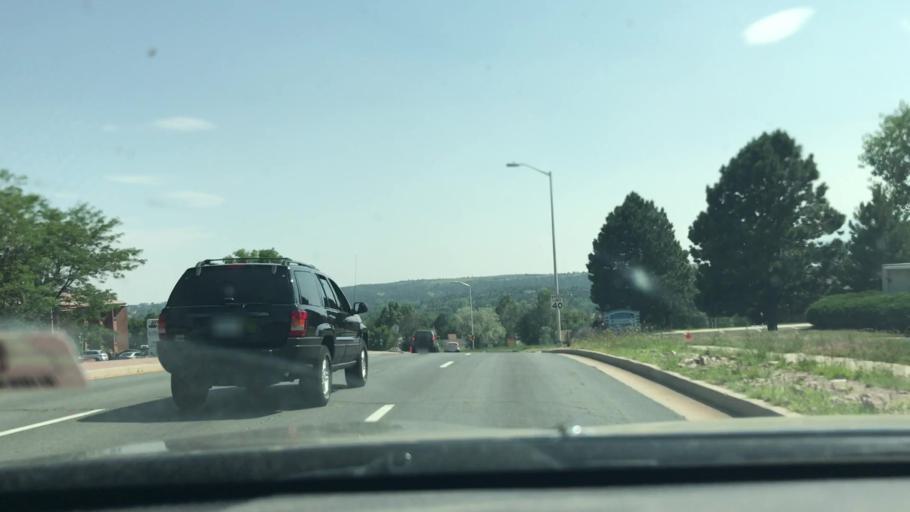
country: US
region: Colorado
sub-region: El Paso County
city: Colorado Springs
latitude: 38.9106
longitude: -104.7754
